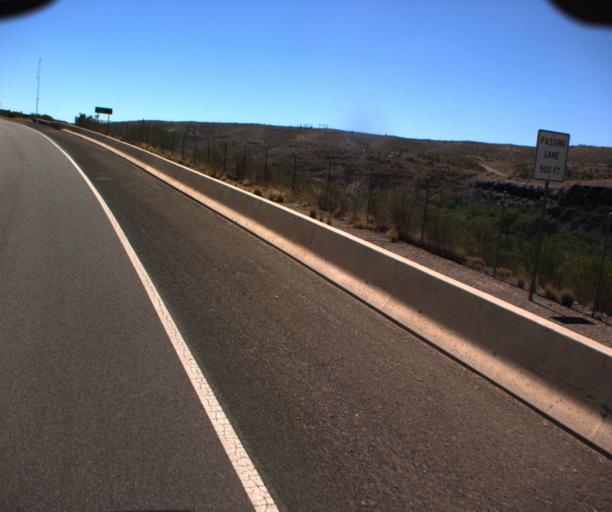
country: US
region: Arizona
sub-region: Greenlee County
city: Clifton
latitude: 33.0400
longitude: -109.2956
